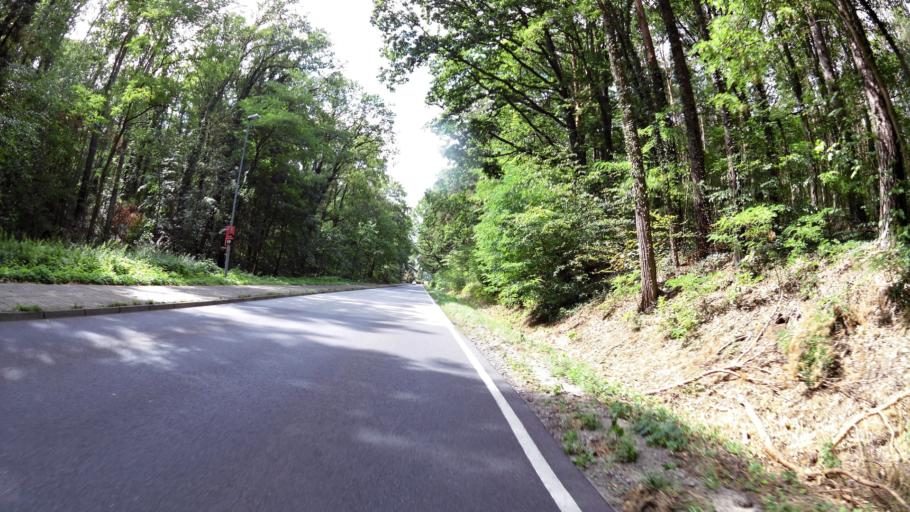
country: DE
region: Brandenburg
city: Neuzelle
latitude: 52.0942
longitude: 14.6408
